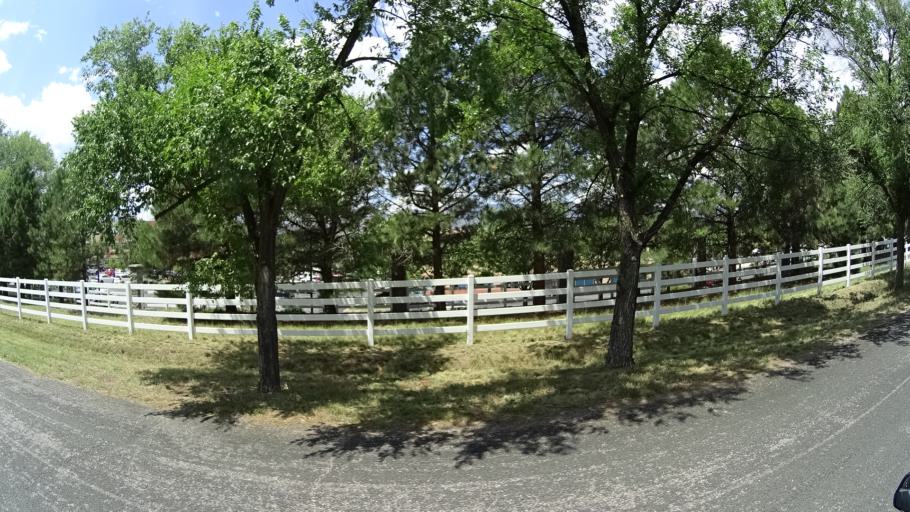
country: US
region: Colorado
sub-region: El Paso County
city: Air Force Academy
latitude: 38.9385
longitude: -104.8106
